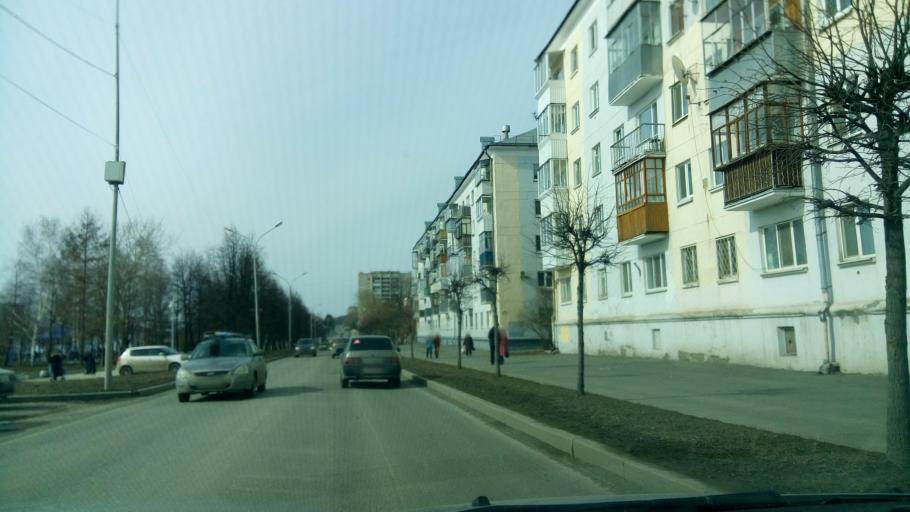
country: RU
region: Sverdlovsk
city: Nizhniy Tagil
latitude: 57.9057
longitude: 59.9821
